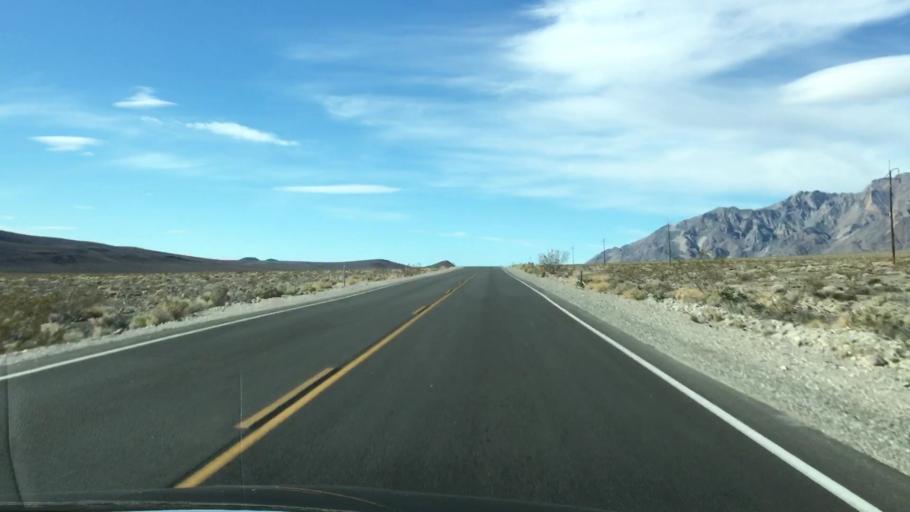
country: US
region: Nevada
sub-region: Nye County
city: Pahrump
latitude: 36.3222
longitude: -116.5571
